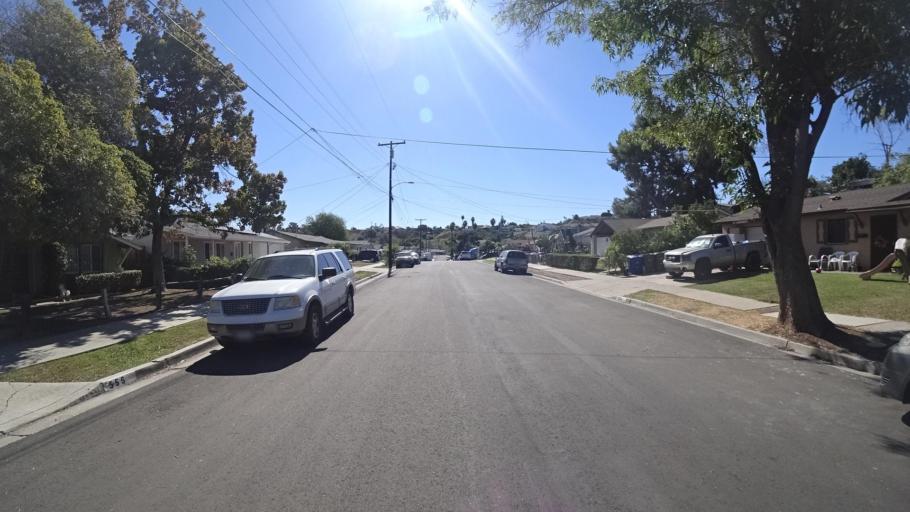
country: US
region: California
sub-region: San Diego County
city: La Presa
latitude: 32.7033
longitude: -117.0195
